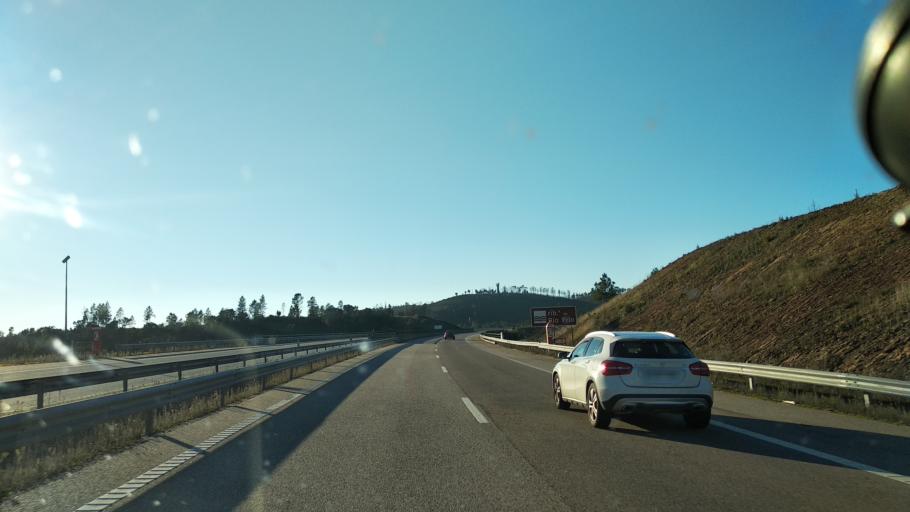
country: PT
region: Santarem
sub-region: Macao
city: Macao
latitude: 39.4926
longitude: -8.0603
